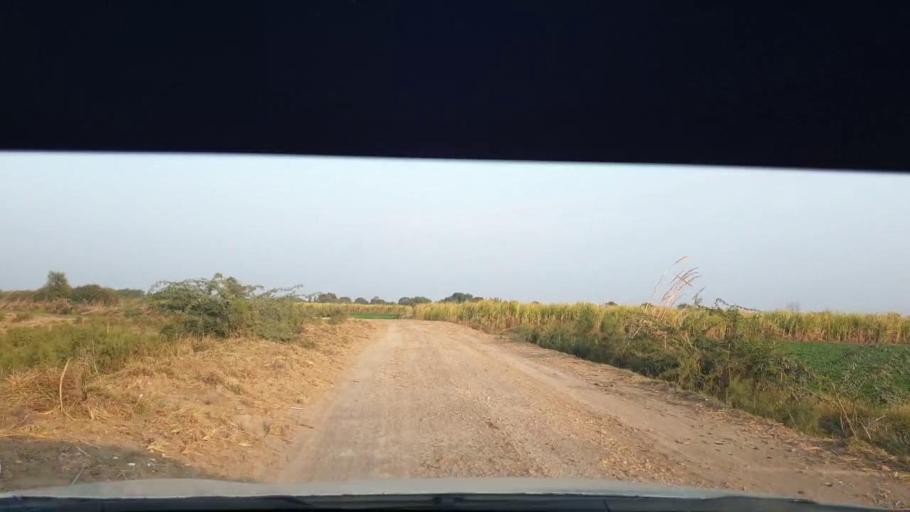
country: PK
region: Sindh
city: Berani
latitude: 25.7400
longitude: 68.9663
